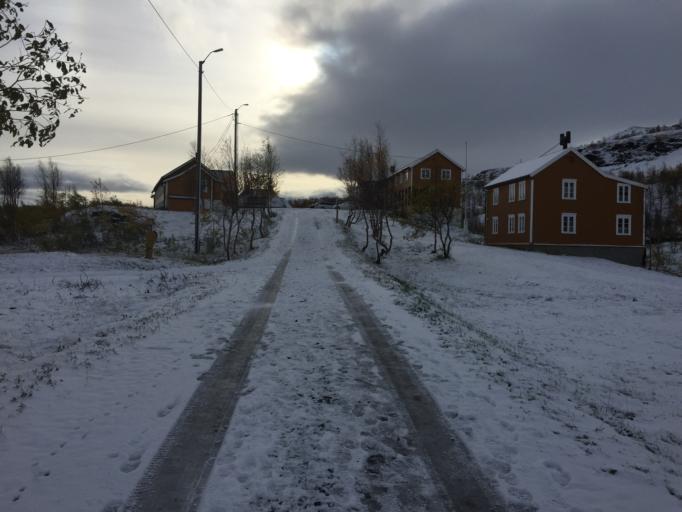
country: NO
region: Nordland
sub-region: Sorfold
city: Straumen
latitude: 67.0954
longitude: 16.0062
